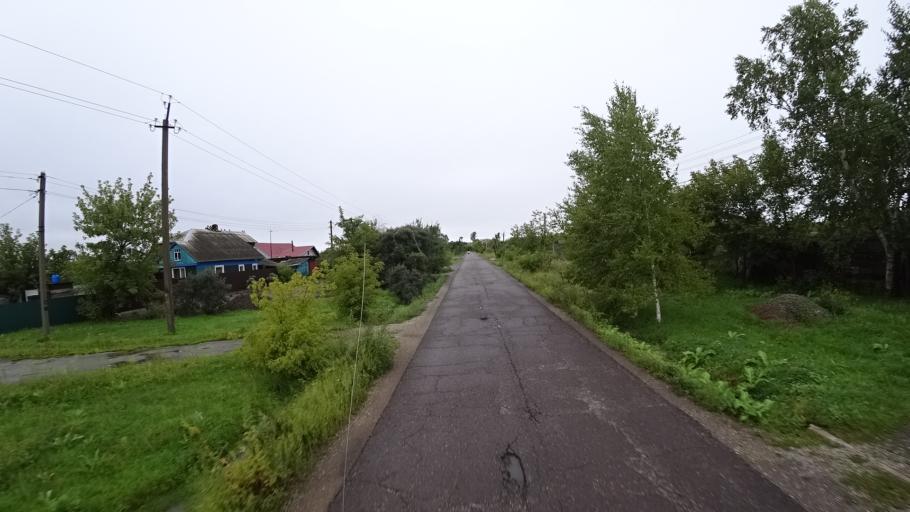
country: RU
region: Primorskiy
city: Monastyrishche
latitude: 44.2011
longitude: 132.4630
